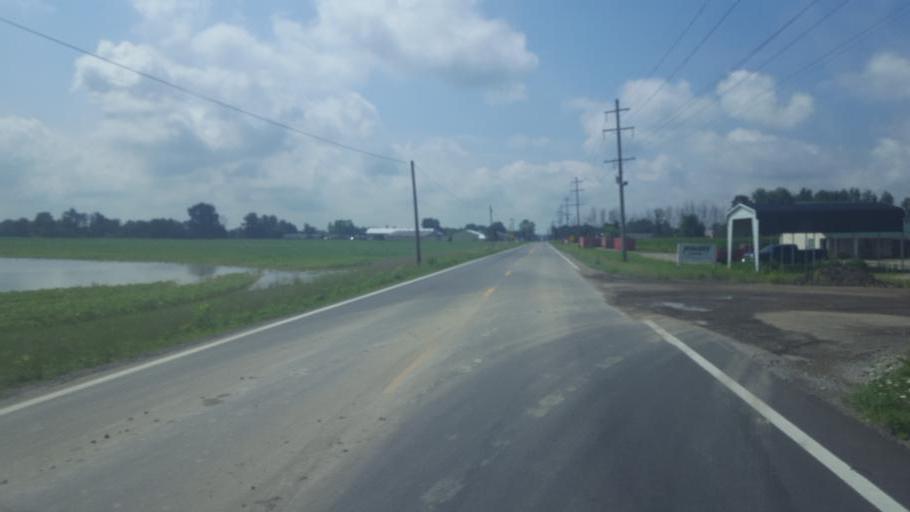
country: US
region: Ohio
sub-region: Fairfield County
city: Baltimore
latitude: 39.8502
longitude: -82.5678
